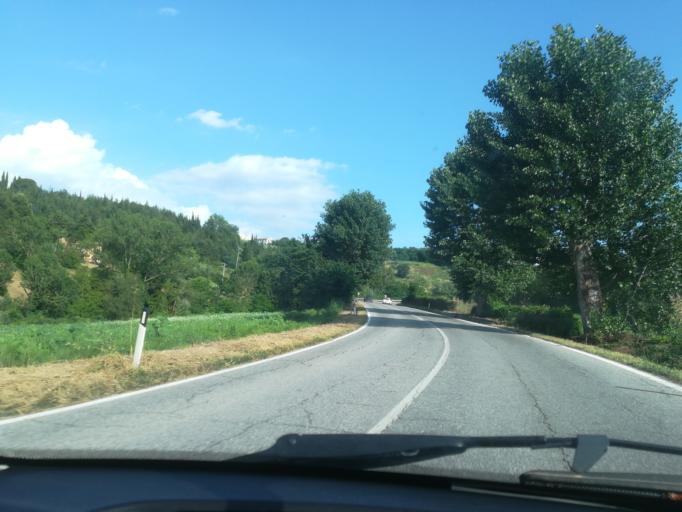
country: IT
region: The Marches
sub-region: Provincia di Macerata
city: Villa Potenza
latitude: 43.3163
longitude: 13.4268
